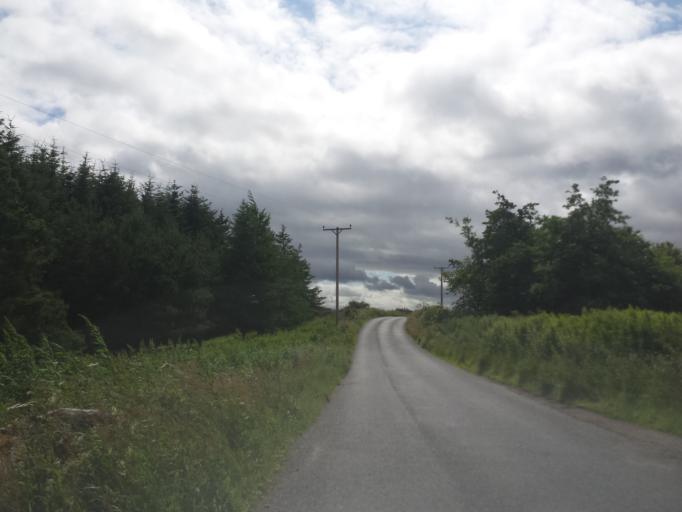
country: GB
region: Scotland
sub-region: Highland
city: Fortrose
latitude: 57.4729
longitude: -4.0893
